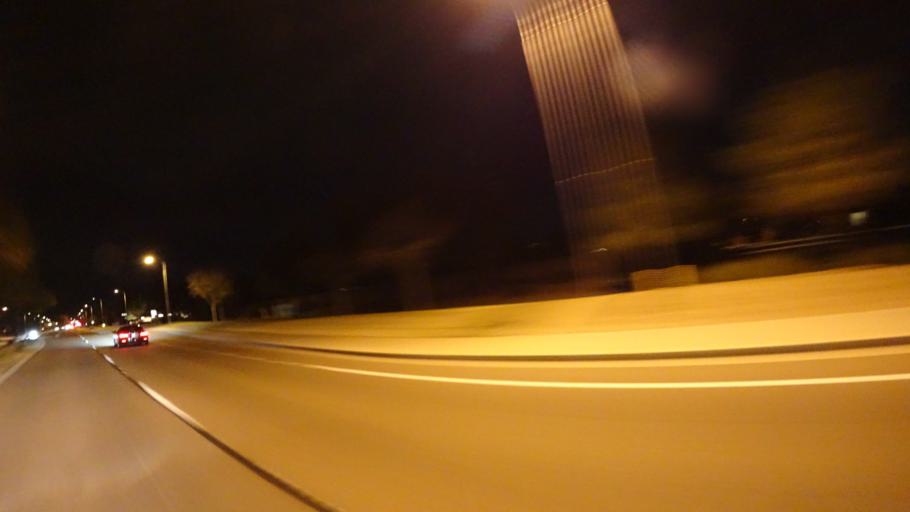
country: US
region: Arizona
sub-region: Maricopa County
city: Chandler
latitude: 33.2480
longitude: -111.8128
